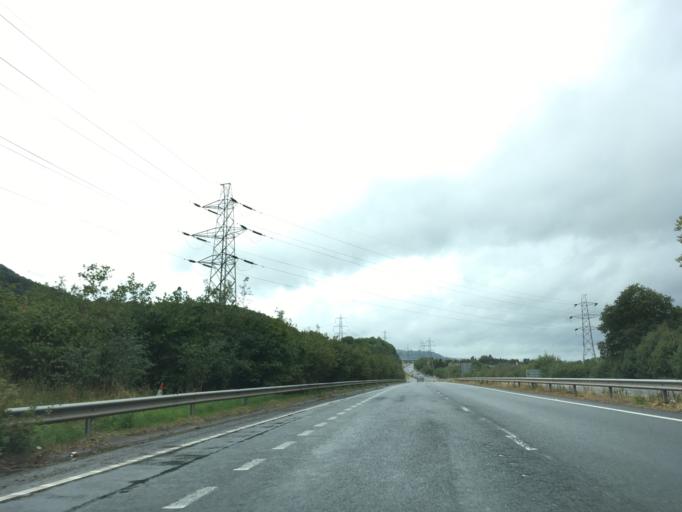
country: GB
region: Wales
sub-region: Monmouthshire
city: Abergavenny
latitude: 51.8166
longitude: -3.0327
